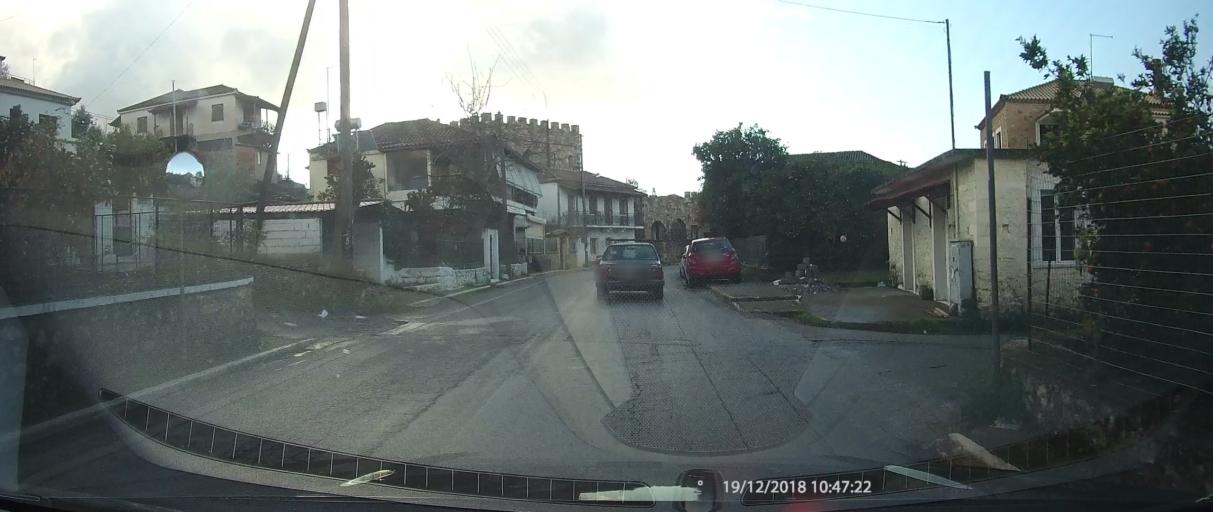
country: GR
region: Peloponnese
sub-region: Nomos Messinias
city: Kardamyli
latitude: 36.9365
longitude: 22.1915
